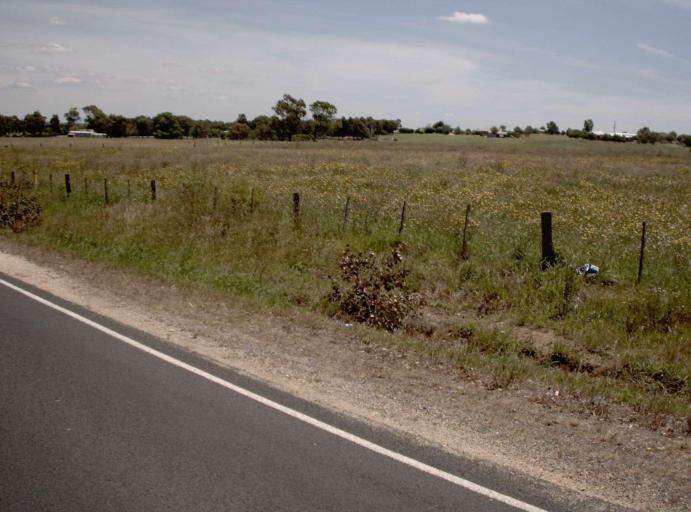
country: AU
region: Victoria
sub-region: East Gippsland
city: Bairnsdale
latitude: -37.8055
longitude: 147.6509
